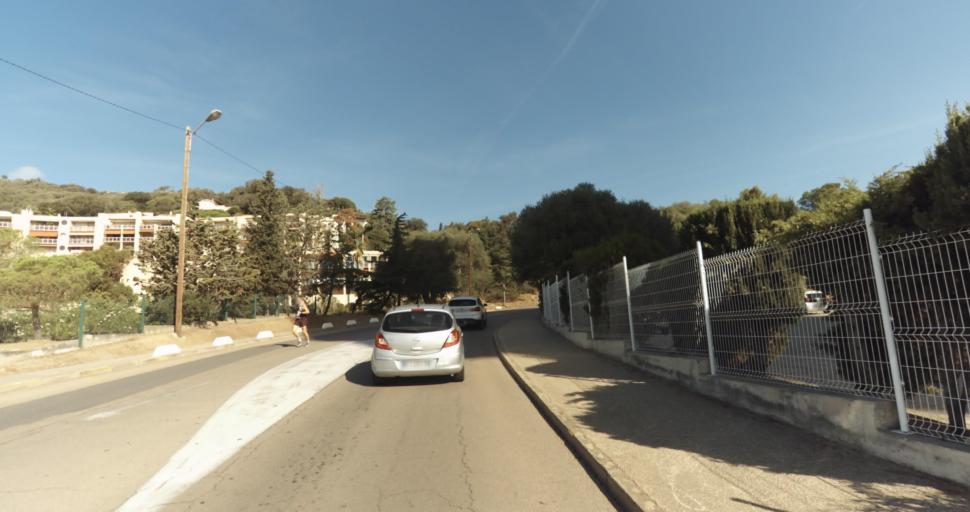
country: FR
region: Corsica
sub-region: Departement de la Corse-du-Sud
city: Ajaccio
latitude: 41.9212
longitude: 8.7300
